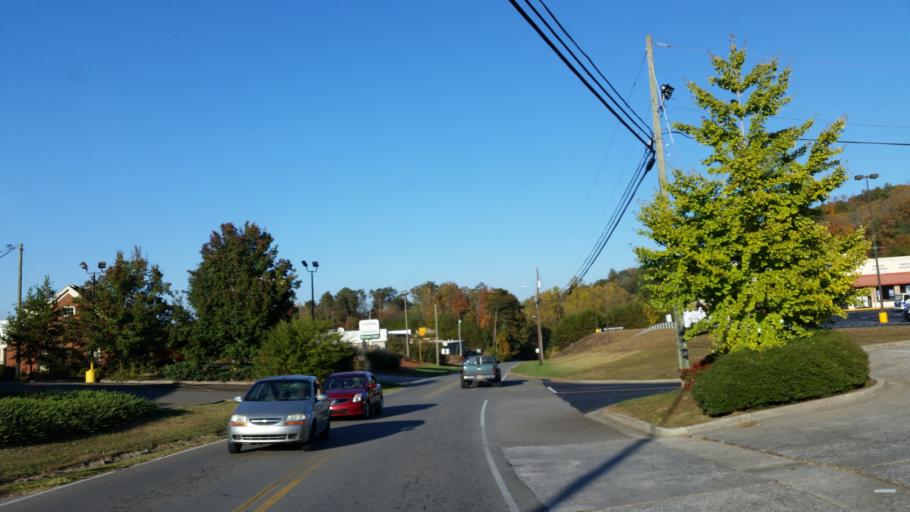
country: US
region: Georgia
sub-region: Gilmer County
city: Ellijay
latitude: 34.6769
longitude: -84.4773
